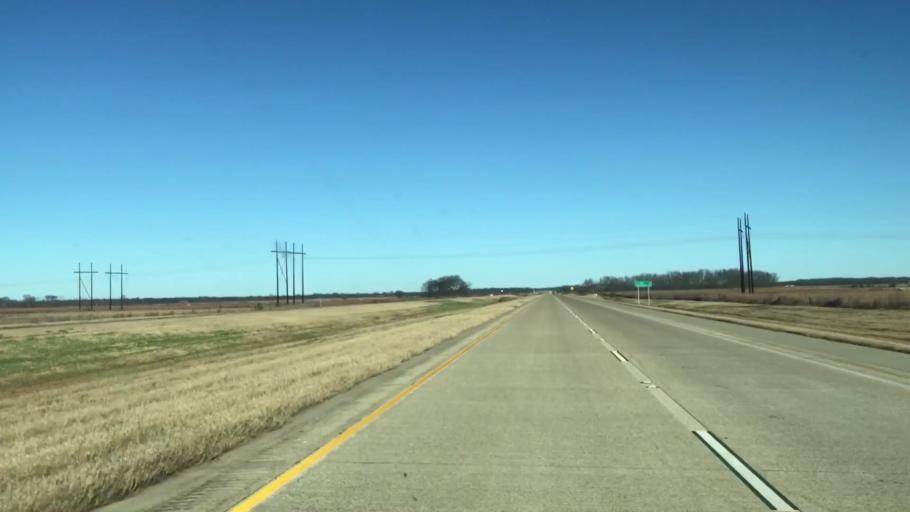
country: US
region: Louisiana
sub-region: Caddo Parish
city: Oil City
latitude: 32.7148
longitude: -93.8664
